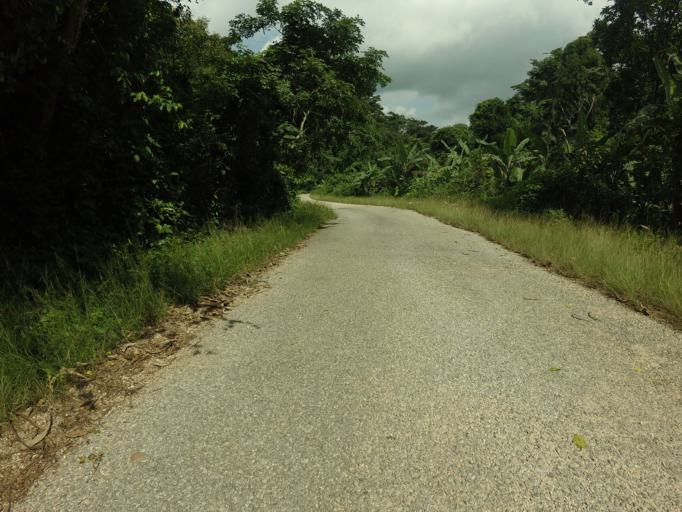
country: GH
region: Volta
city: Kpandu
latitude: 6.8319
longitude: 0.4241
